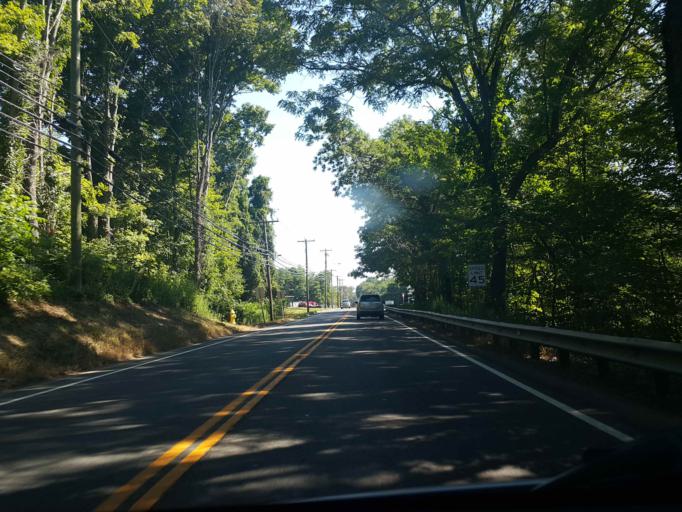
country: US
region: Connecticut
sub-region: New Haven County
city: North Branford
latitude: 41.3308
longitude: -72.7616
